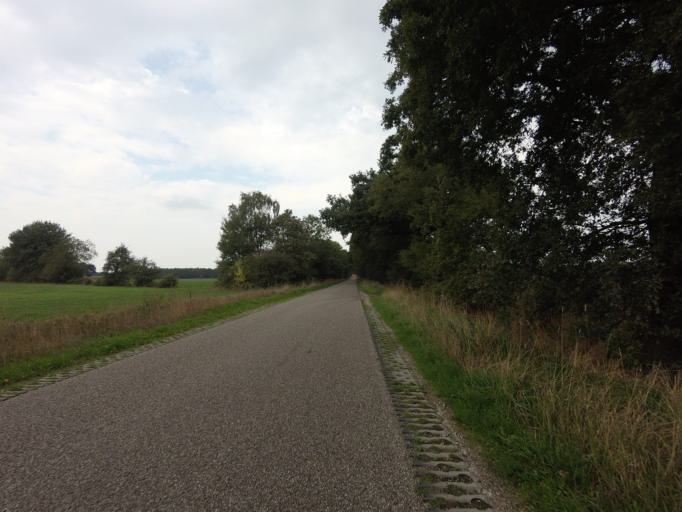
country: NL
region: Drenthe
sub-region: Gemeente Tynaarlo
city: Vries
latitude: 53.0437
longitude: 6.5959
